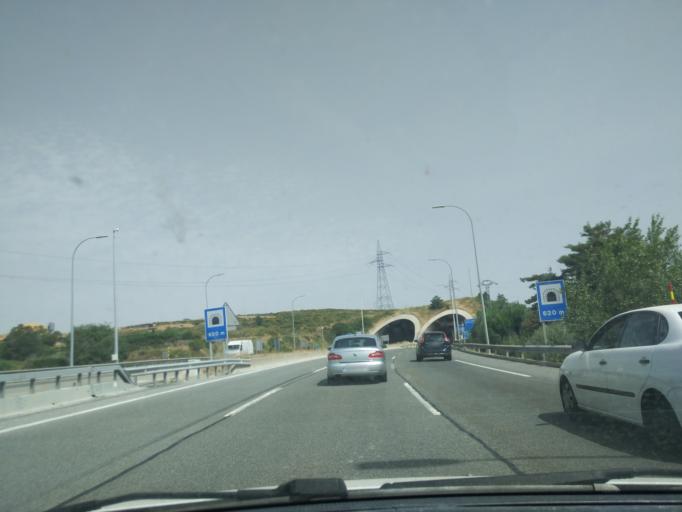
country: ES
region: Madrid
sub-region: Provincia de Madrid
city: Somosierra
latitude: 41.1298
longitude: -3.5839
